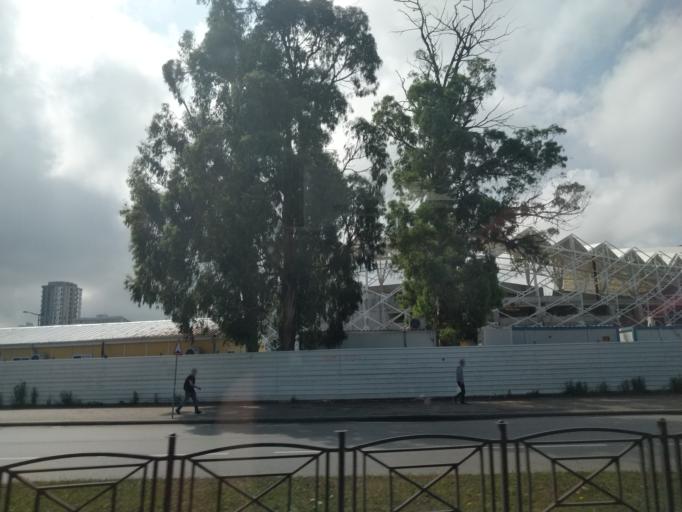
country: GE
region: Ajaria
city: Batumi
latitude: 41.6369
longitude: 41.6182
